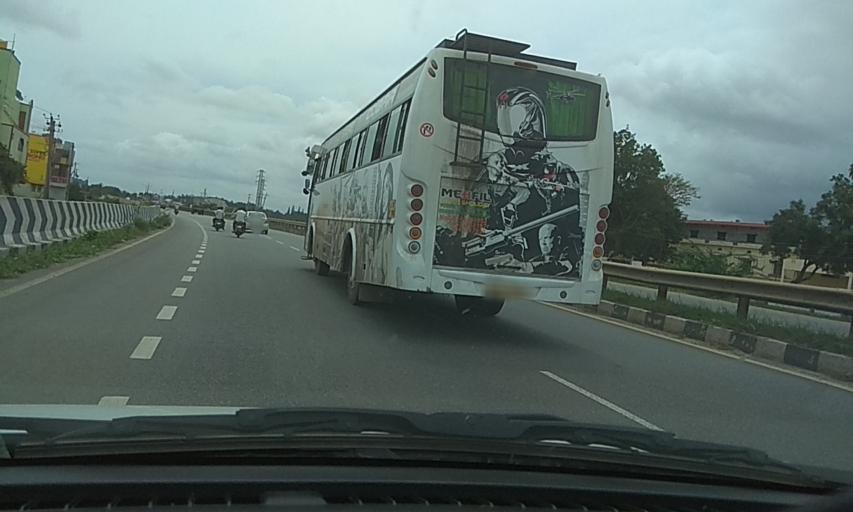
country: IN
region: Karnataka
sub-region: Chitradurga
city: Chitradurga
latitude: 14.2387
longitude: 76.3772
